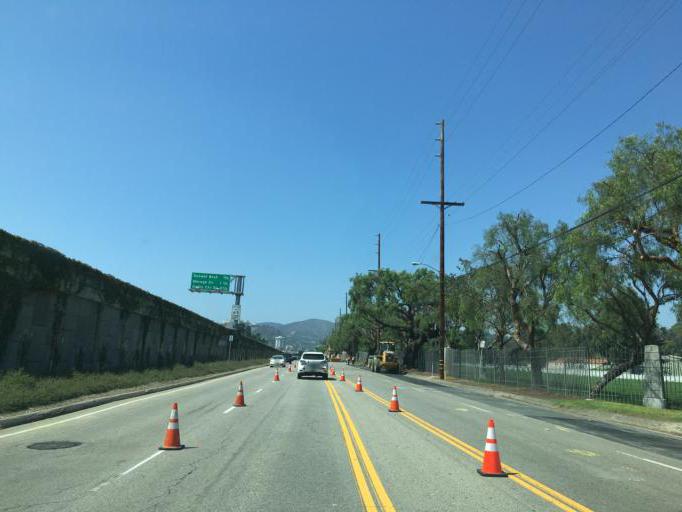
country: US
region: California
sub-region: Los Angeles County
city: Westwood, Los Angeles
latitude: 34.0606
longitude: -118.4555
